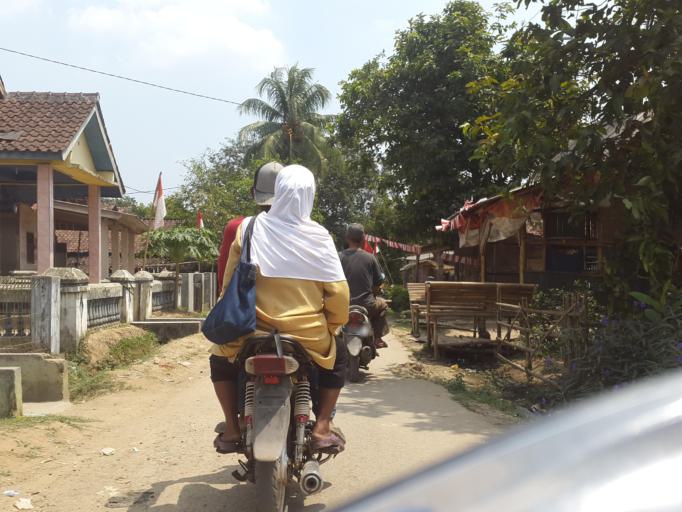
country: ID
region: West Java
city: Cikupa
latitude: -6.3582
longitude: 106.4277
